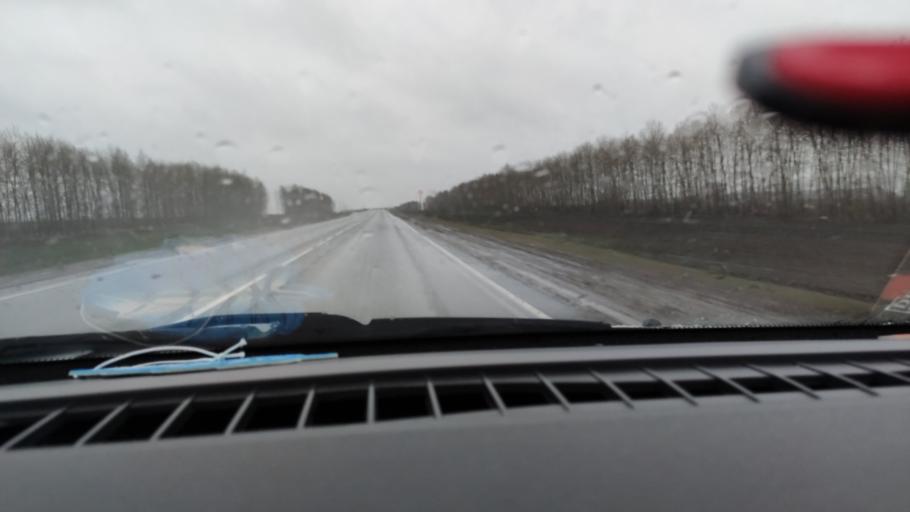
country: RU
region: Tatarstan
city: Mendeleyevsk
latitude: 55.9284
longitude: 52.2798
